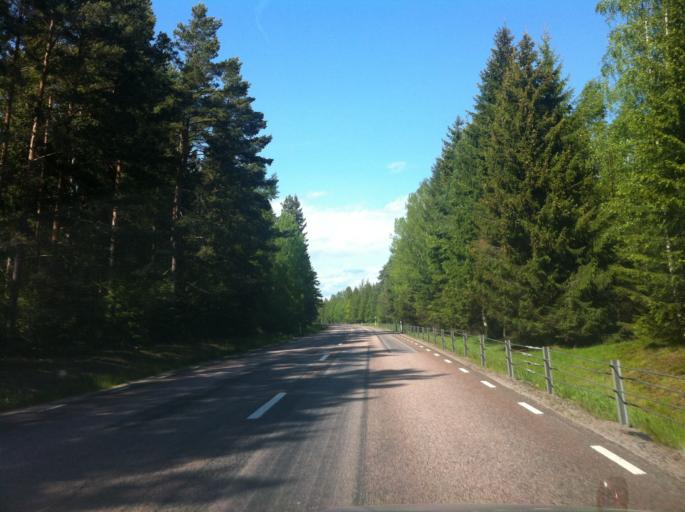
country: SE
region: Vaestra Goetaland
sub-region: Gullspangs Kommun
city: Gullspang
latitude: 59.0738
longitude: 14.1554
